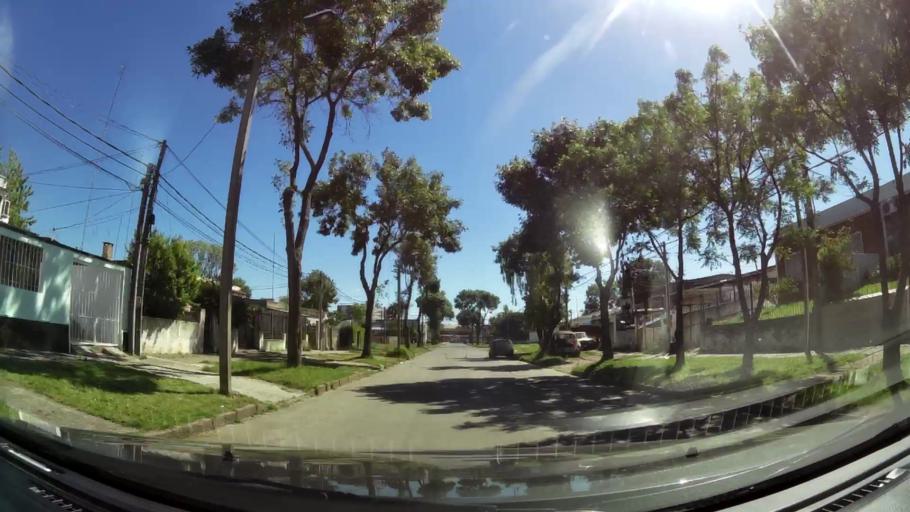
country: UY
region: Canelones
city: Paso de Carrasco
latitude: -34.8626
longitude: -56.1250
